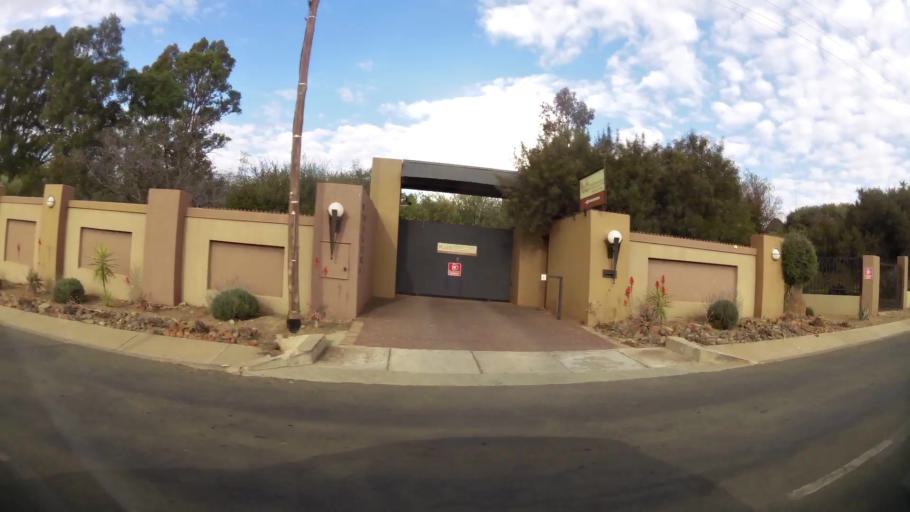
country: ZA
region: Orange Free State
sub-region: Mangaung Metropolitan Municipality
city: Bloemfontein
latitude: -29.0743
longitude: 26.1928
